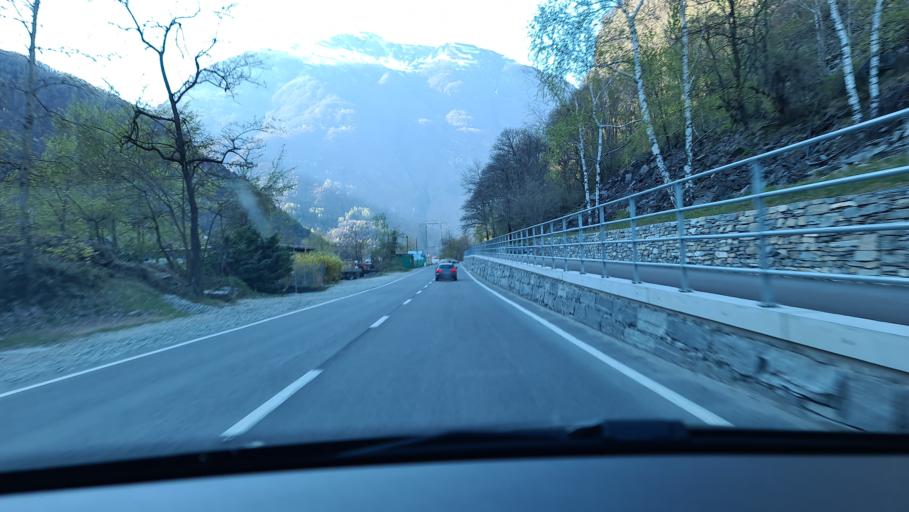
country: CH
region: Ticino
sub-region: Vallemaggia District
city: Cevio
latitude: 46.3013
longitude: 8.6210
